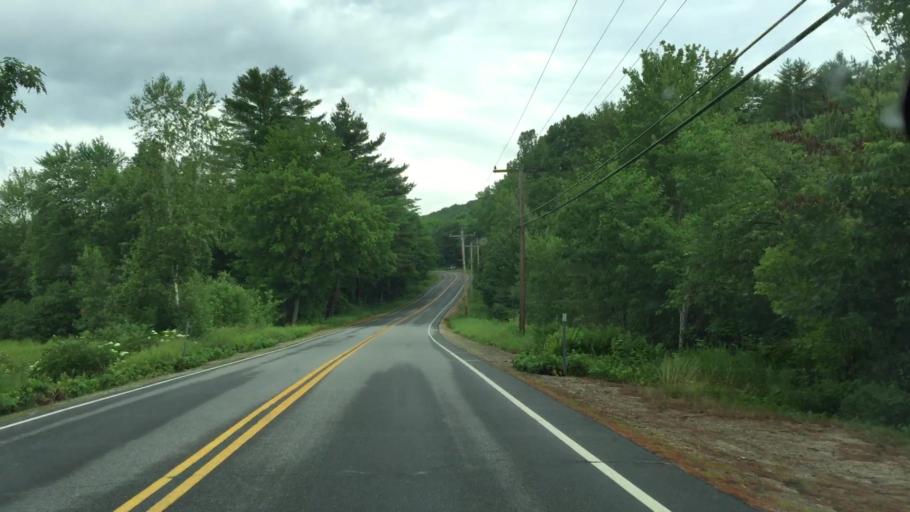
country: US
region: New Hampshire
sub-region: Carroll County
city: Center Harbor
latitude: 43.7435
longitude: -71.4781
